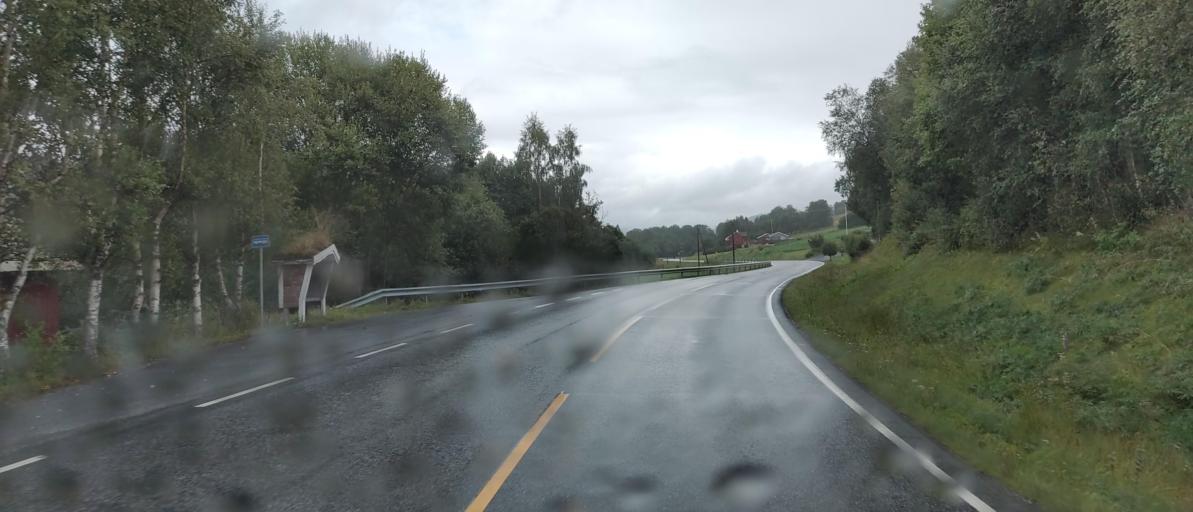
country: NO
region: More og Romsdal
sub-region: Tingvoll
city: Tingvoll
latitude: 63.0428
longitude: 8.0488
